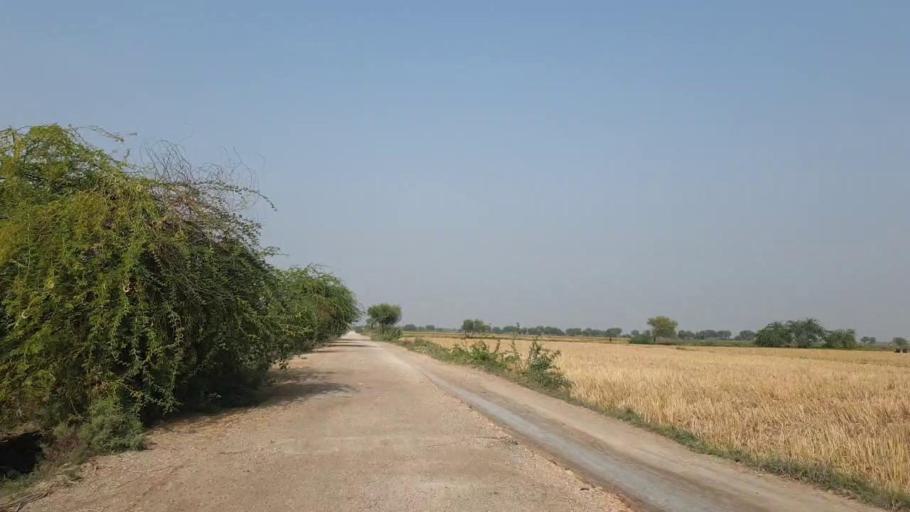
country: PK
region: Sindh
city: Kario
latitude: 24.9393
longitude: 68.5573
